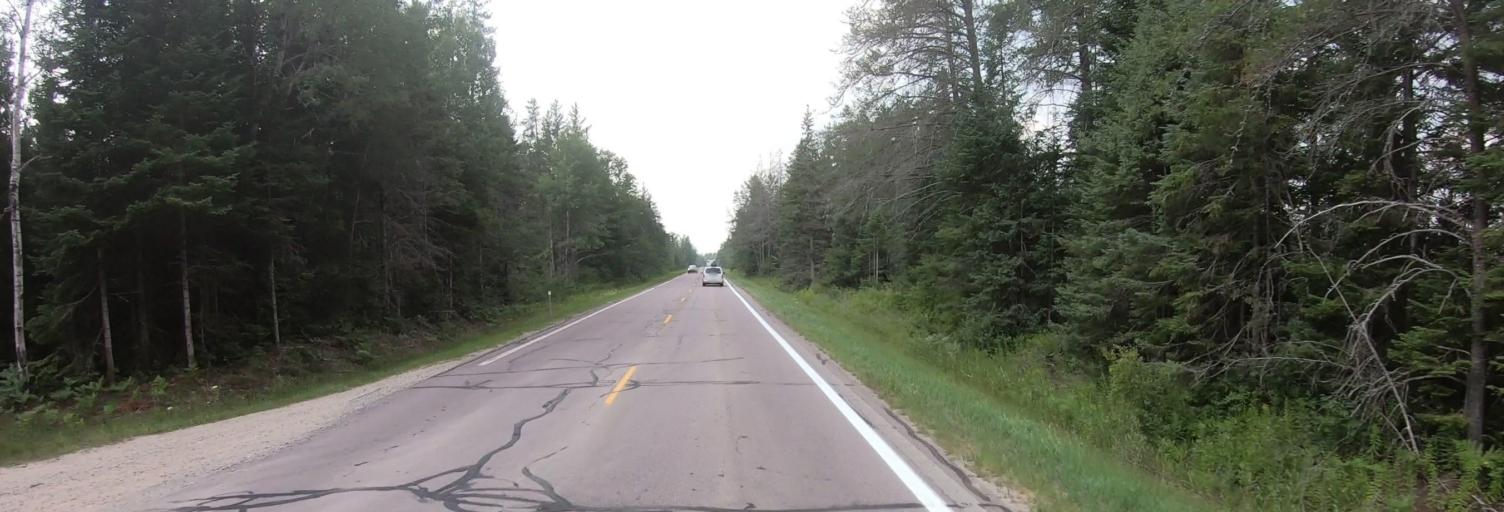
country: US
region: Michigan
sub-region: Luce County
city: Newberry
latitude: 46.4693
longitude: -85.4307
